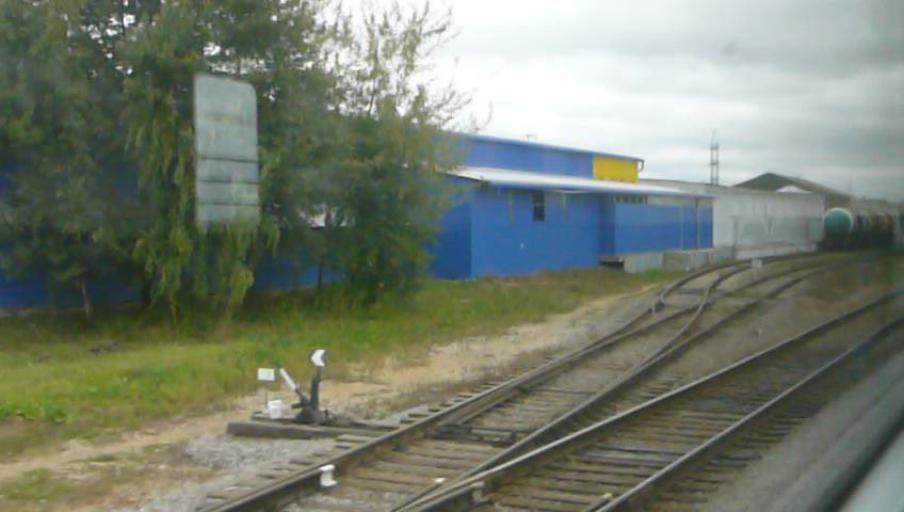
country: RU
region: Moskovskaya
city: Yegor'yevsk
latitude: 55.3943
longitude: 39.0057
